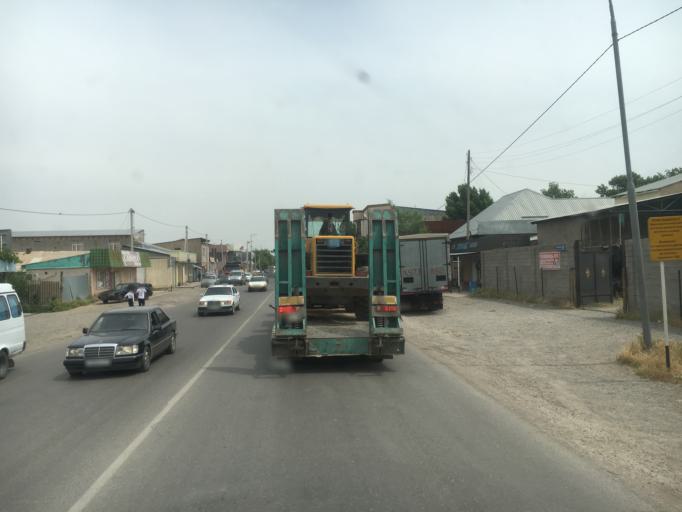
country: KZ
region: Ongtustik Qazaqstan
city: Shymkent
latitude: 42.3396
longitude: 69.5213
